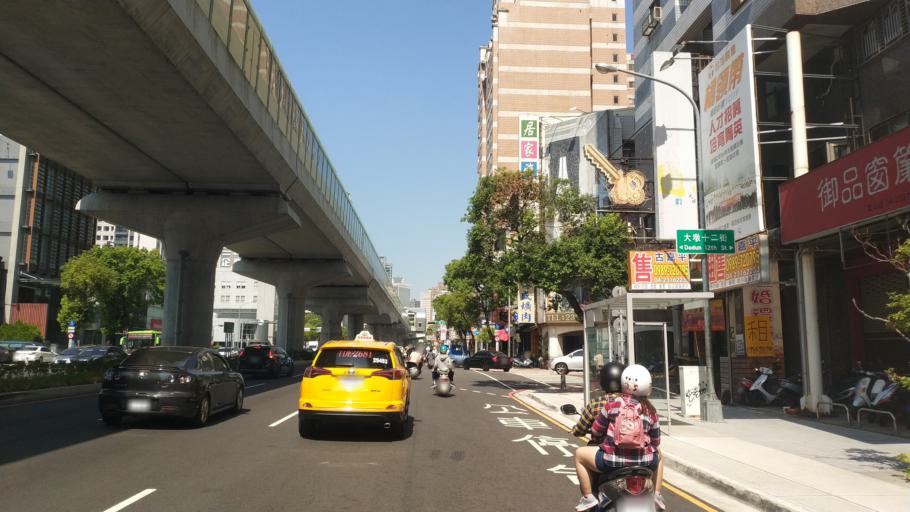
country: TW
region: Taiwan
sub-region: Taichung City
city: Taichung
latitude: 24.1496
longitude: 120.6468
